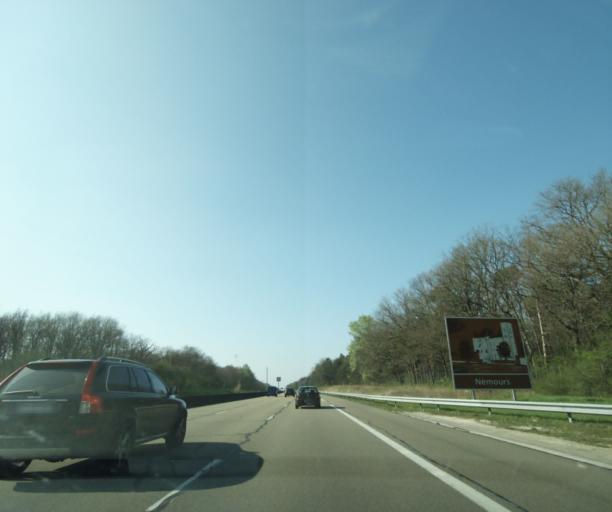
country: FR
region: Ile-de-France
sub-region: Departement de Seine-et-Marne
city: Bagneaux-sur-Loing
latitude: 48.2433
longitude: 2.7466
